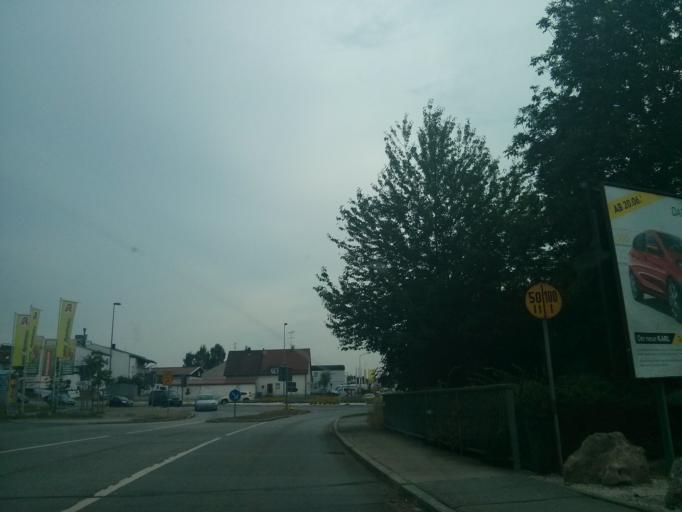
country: DE
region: Bavaria
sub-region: Lower Bavaria
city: Deggendorf
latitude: 48.8541
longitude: 12.9623
